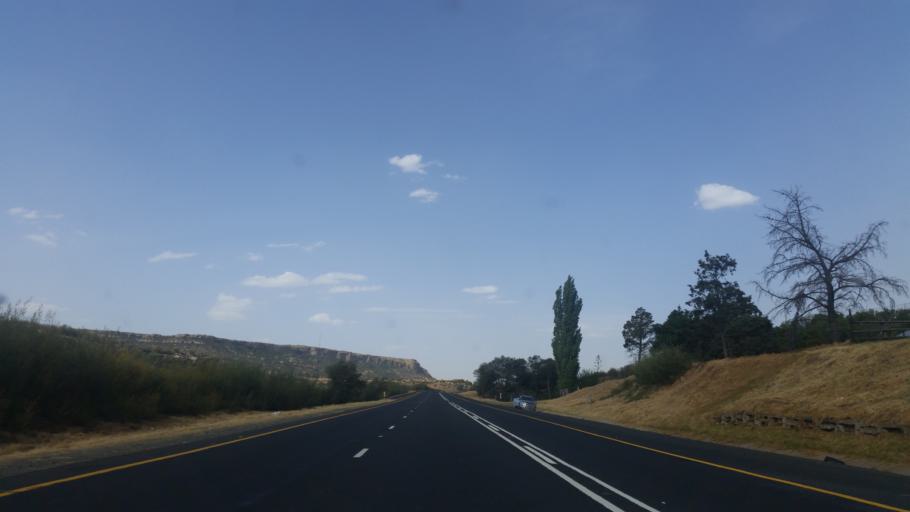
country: ZA
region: Orange Free State
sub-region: Thabo Mofutsanyana District Municipality
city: Bethlehem
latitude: -28.2941
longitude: 28.5181
